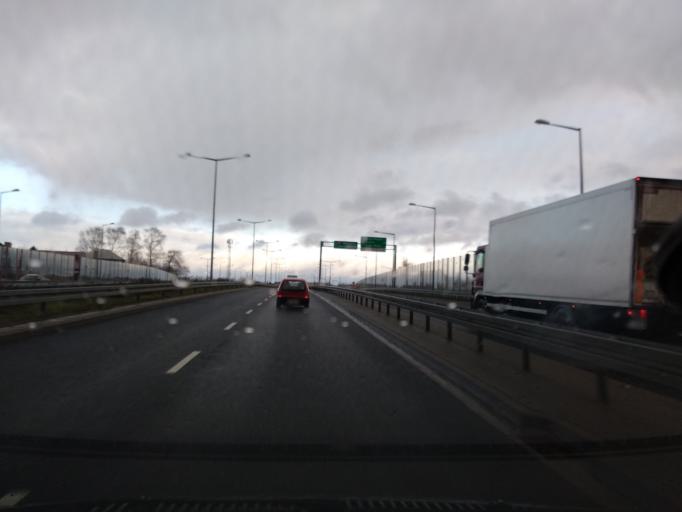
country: PL
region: Greater Poland Voivodeship
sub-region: Powiat koninski
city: Stare Miasto
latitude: 52.1787
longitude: 18.2218
